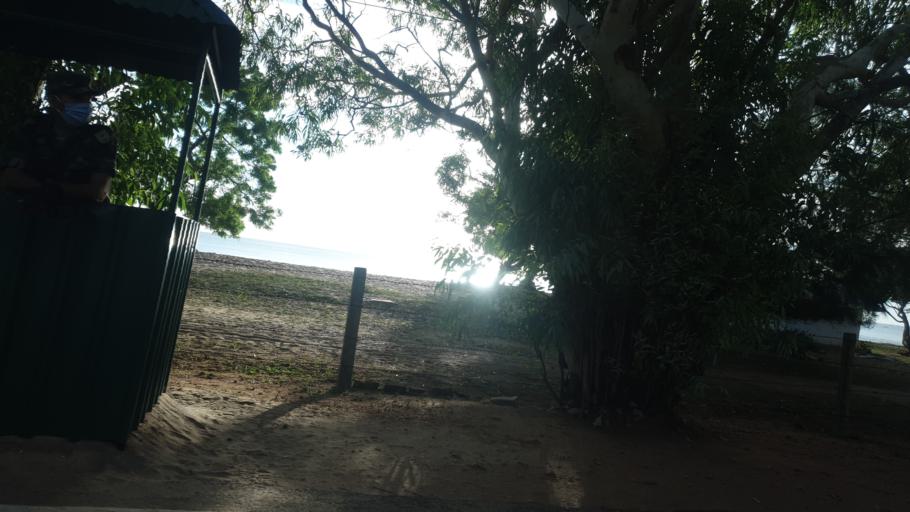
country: LK
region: Eastern Province
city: Trincomalee
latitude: 8.4777
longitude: 81.1972
